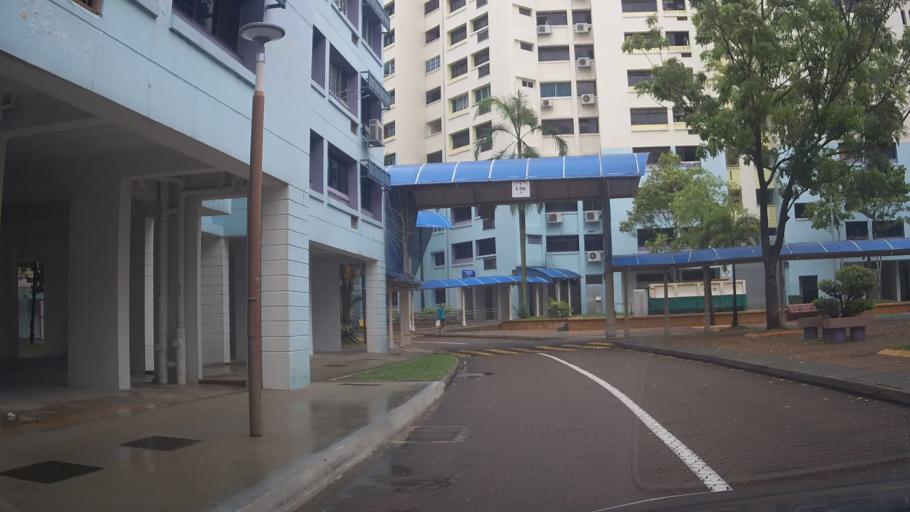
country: MY
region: Johor
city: Johor Bahru
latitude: 1.4408
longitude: 103.7972
